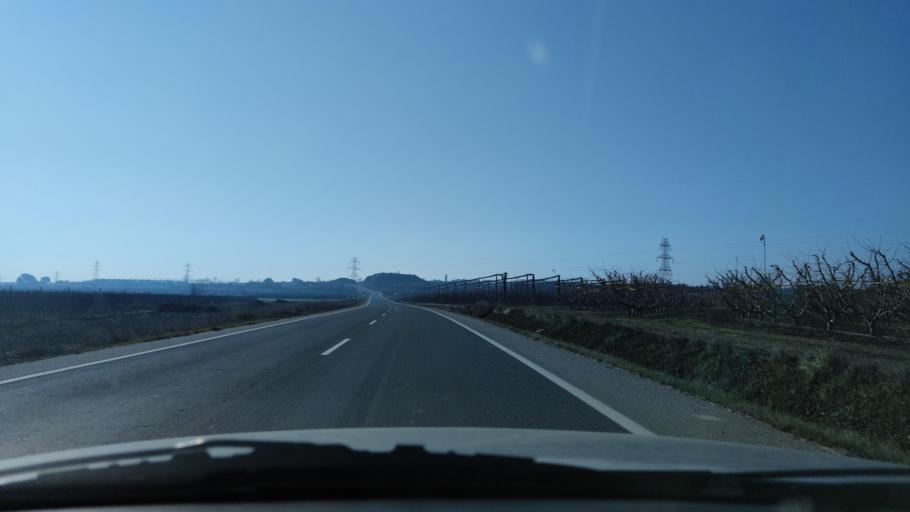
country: ES
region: Catalonia
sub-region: Provincia de Lleida
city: Torrefarrera
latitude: 41.7090
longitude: 0.6380
